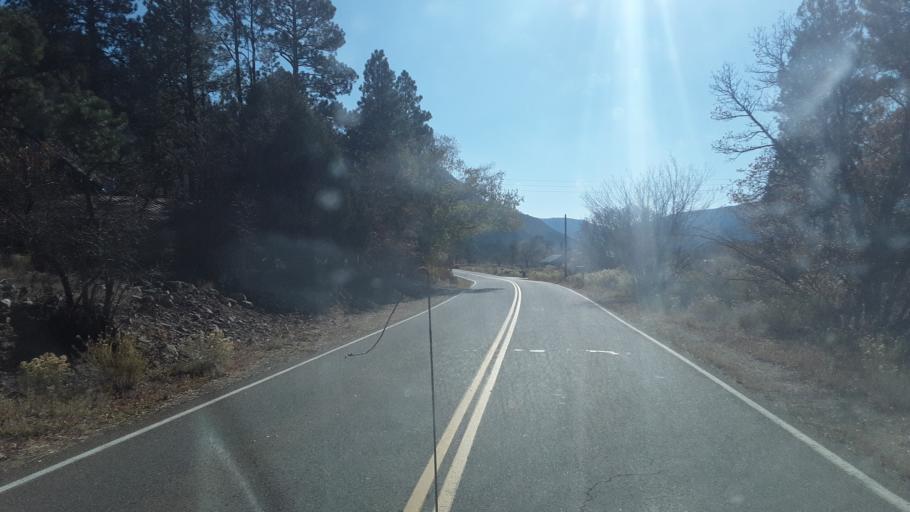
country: US
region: Colorado
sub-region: La Plata County
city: Durango
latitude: 37.4101
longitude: -107.8129
